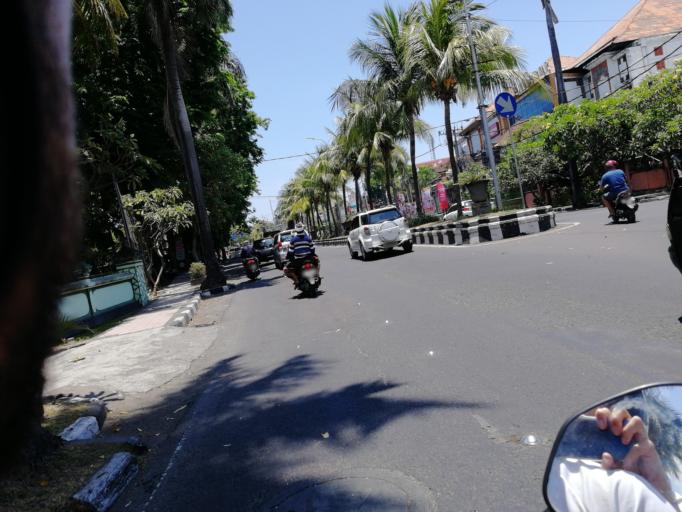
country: ID
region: Bali
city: Denpasar
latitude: -8.6684
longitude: 115.2180
